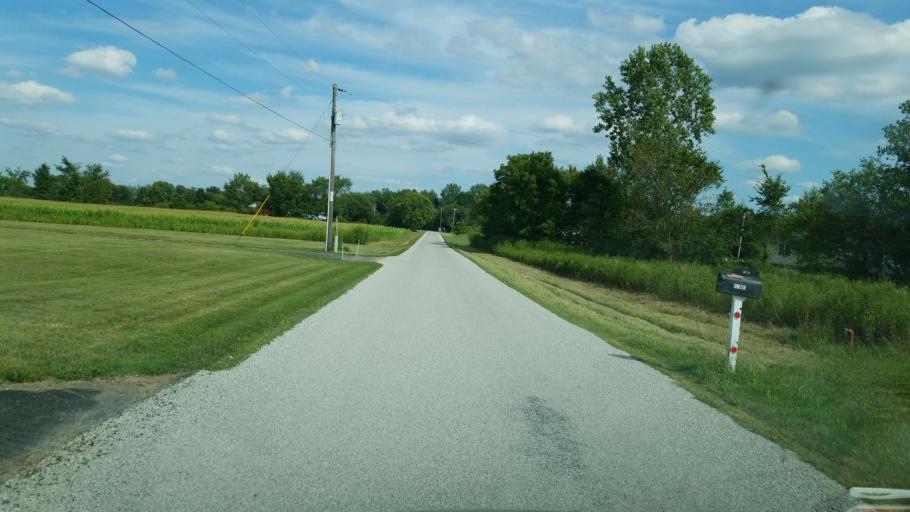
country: US
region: Ohio
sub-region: Delaware County
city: Ashley
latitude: 40.4342
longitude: -83.0030
